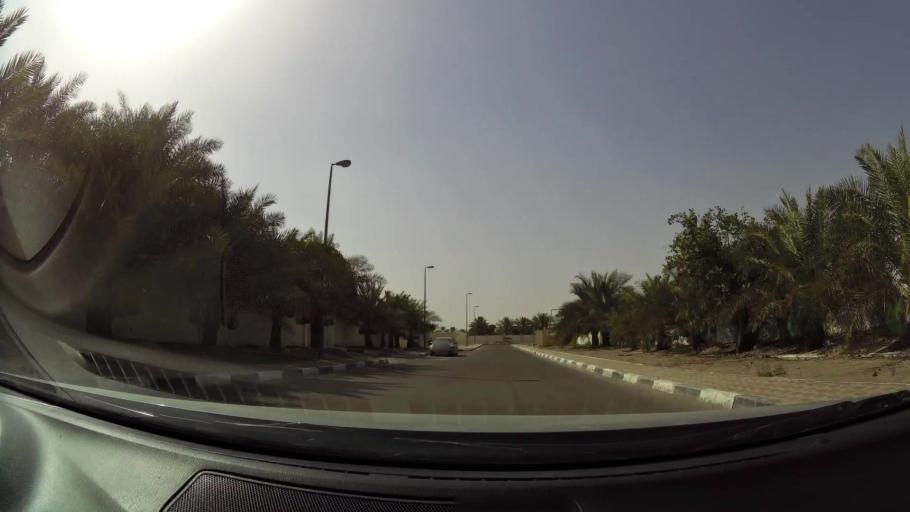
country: AE
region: Abu Dhabi
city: Al Ain
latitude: 24.2417
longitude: 55.6949
